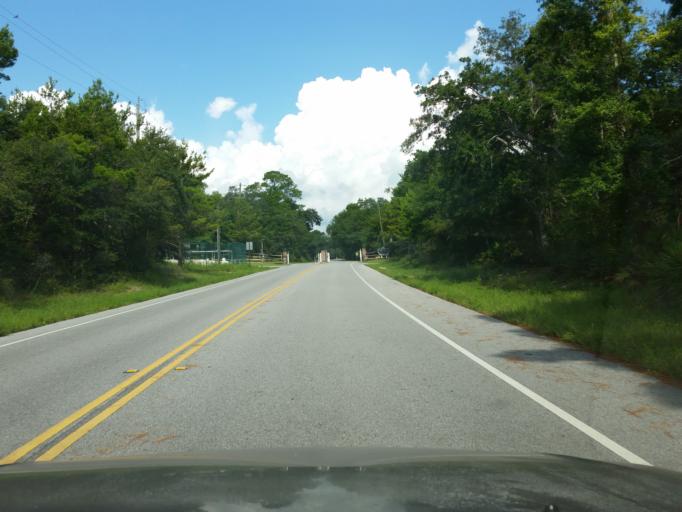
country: US
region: Alabama
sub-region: Baldwin County
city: Orange Beach
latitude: 30.3144
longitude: -87.4771
